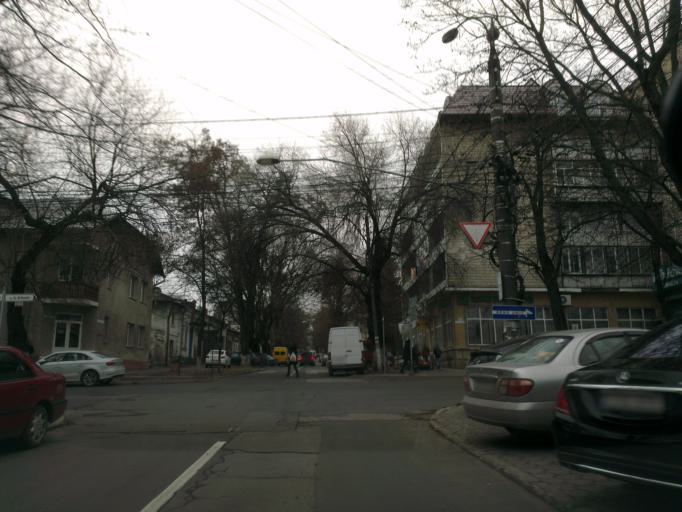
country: MD
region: Chisinau
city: Chisinau
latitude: 47.0189
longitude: 28.8299
